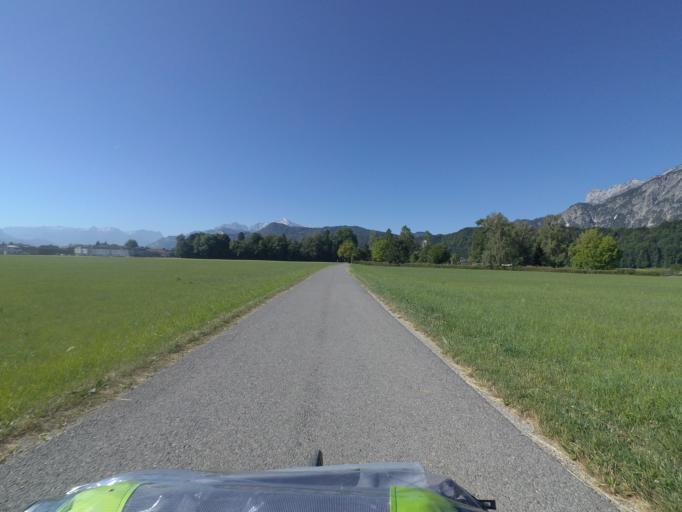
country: AT
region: Salzburg
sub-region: Politischer Bezirk Salzburg-Umgebung
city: Anif
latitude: 47.7347
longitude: 13.0607
